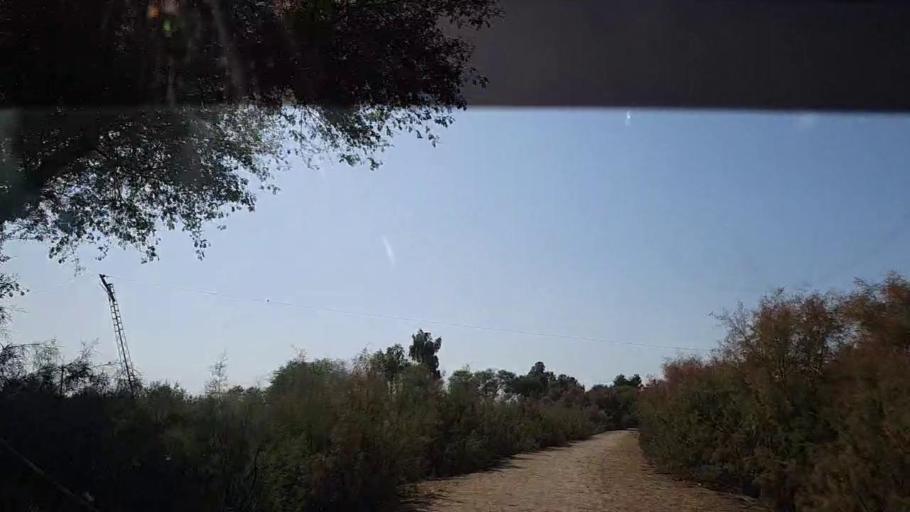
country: PK
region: Sindh
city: Ghauspur
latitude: 28.1798
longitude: 69.0285
